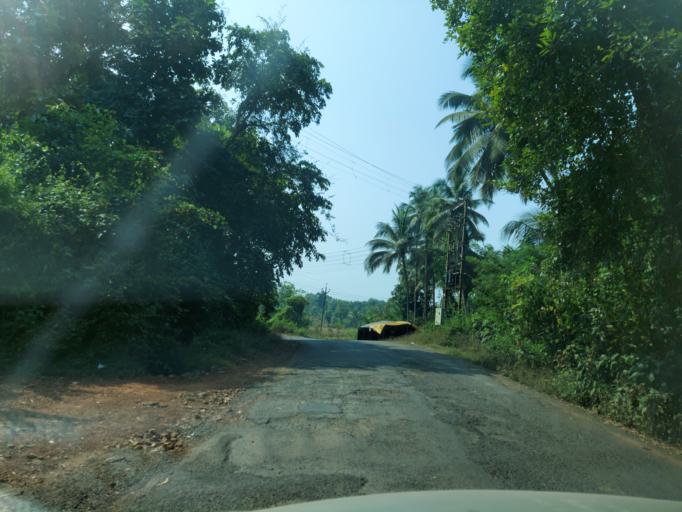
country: IN
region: Maharashtra
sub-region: Sindhudurg
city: Kudal
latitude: 15.9742
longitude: 73.6109
